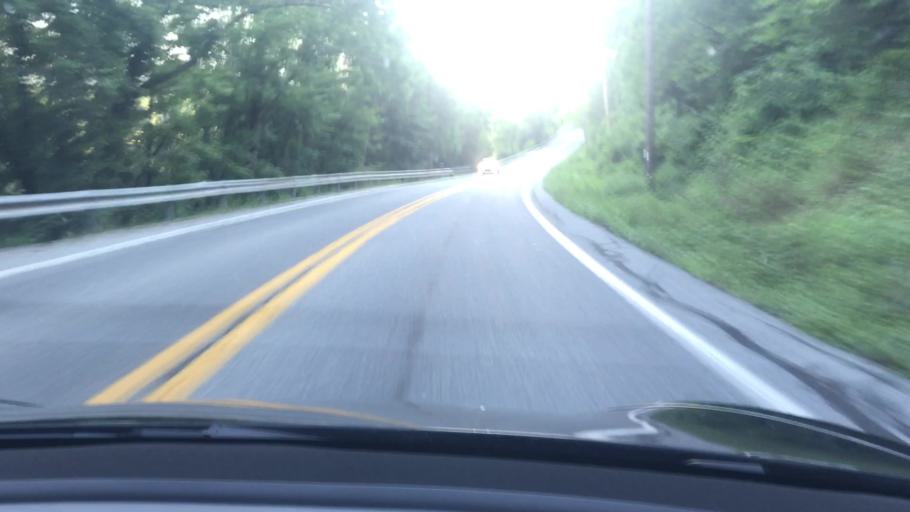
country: US
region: Pennsylvania
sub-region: York County
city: Dover
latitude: 40.0643
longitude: -76.8828
